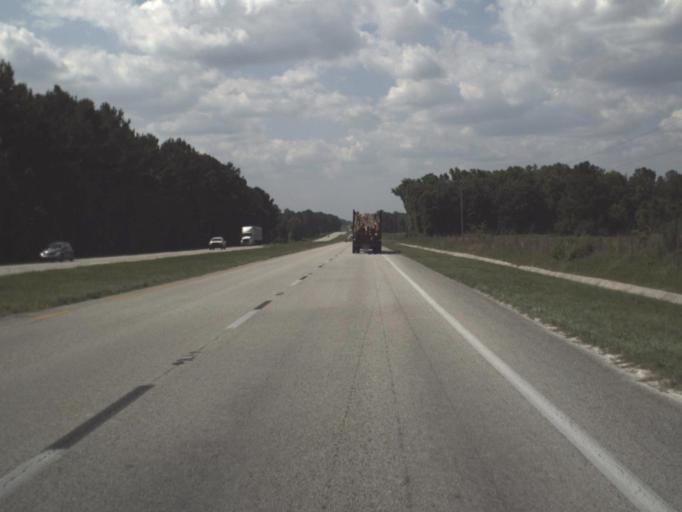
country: US
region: Florida
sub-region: Alachua County
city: Hawthorne
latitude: 29.6702
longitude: -82.1193
